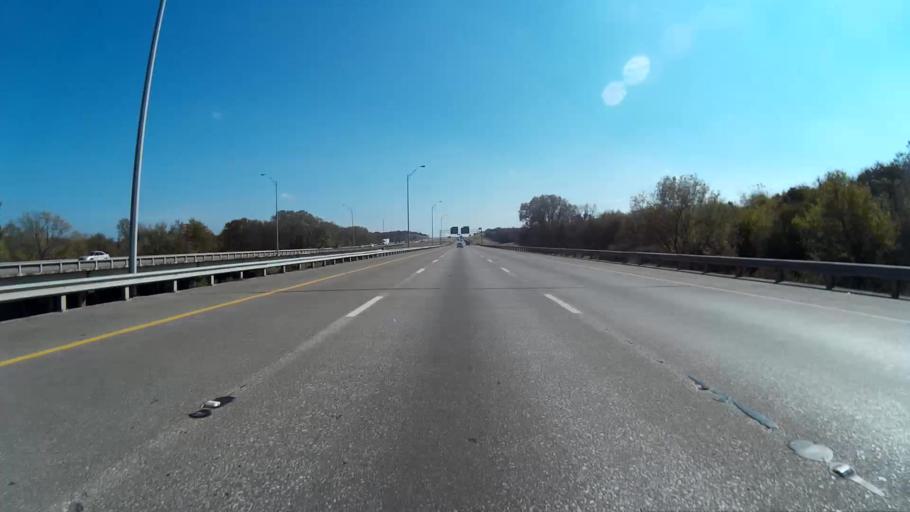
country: US
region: Texas
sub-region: Dallas County
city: Hutchins
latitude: 32.6778
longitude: -96.7411
